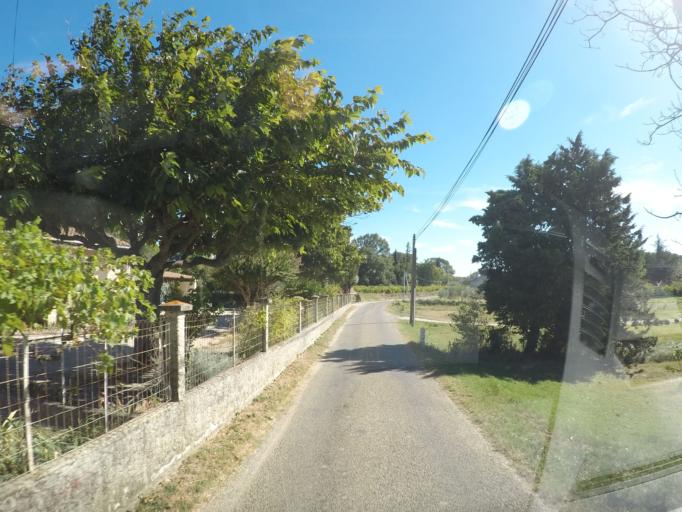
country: FR
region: Rhone-Alpes
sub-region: Departement de la Drome
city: Suze-la-Rousse
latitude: 44.2949
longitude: 4.8269
